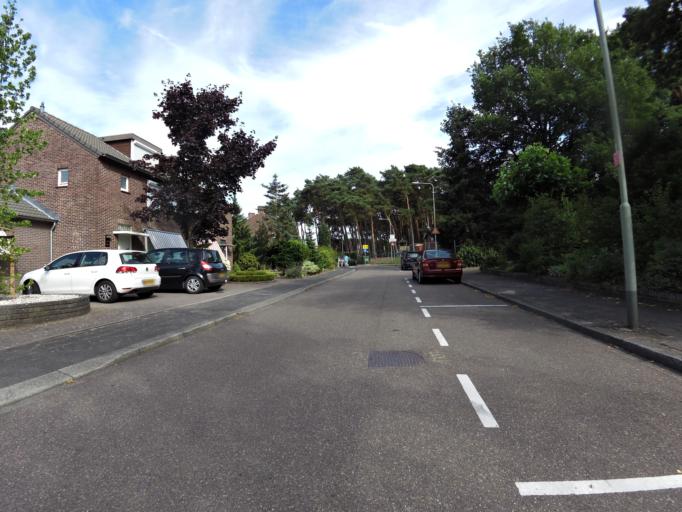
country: NL
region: Limburg
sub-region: Gemeente Onderbanken
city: Schinveld
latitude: 50.9636
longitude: 5.9826
